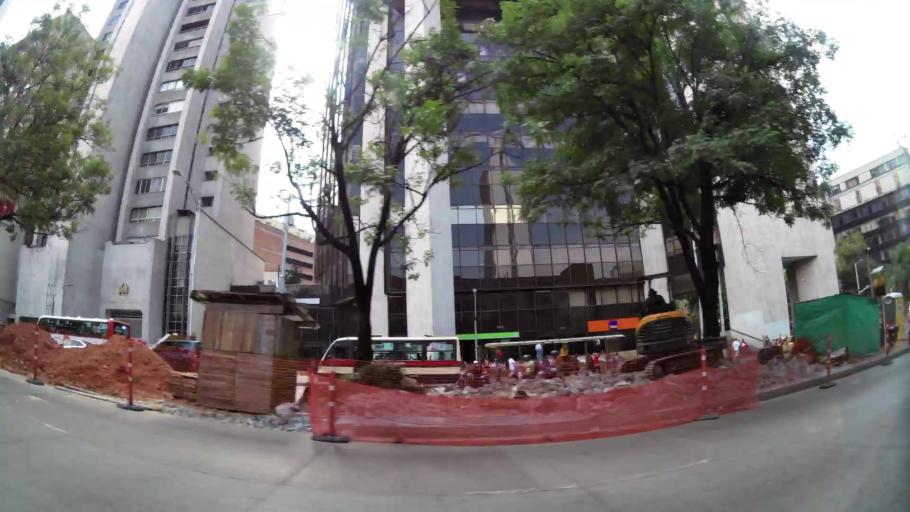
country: CO
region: Antioquia
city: Medellin
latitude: 6.2497
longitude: -75.5646
